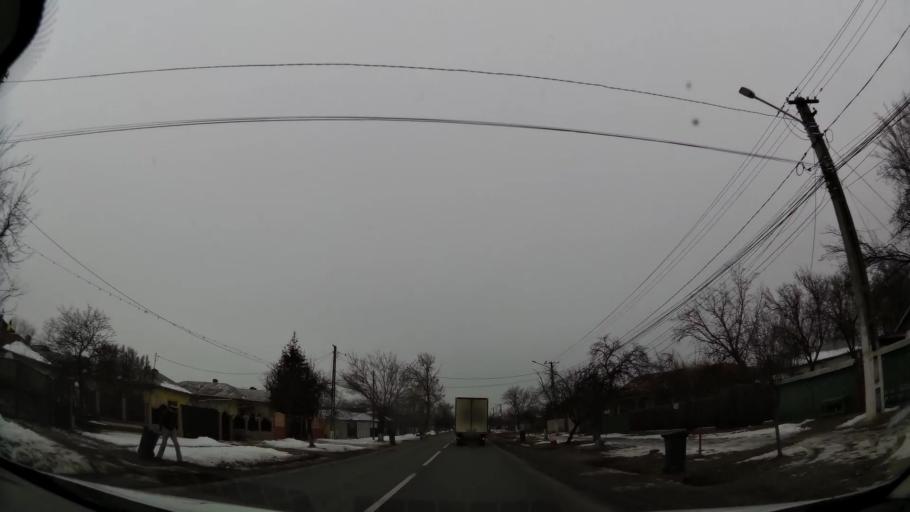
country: RO
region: Dambovita
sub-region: Comuna Tartasesti
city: Baldana
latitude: 44.6155
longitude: 25.7631
